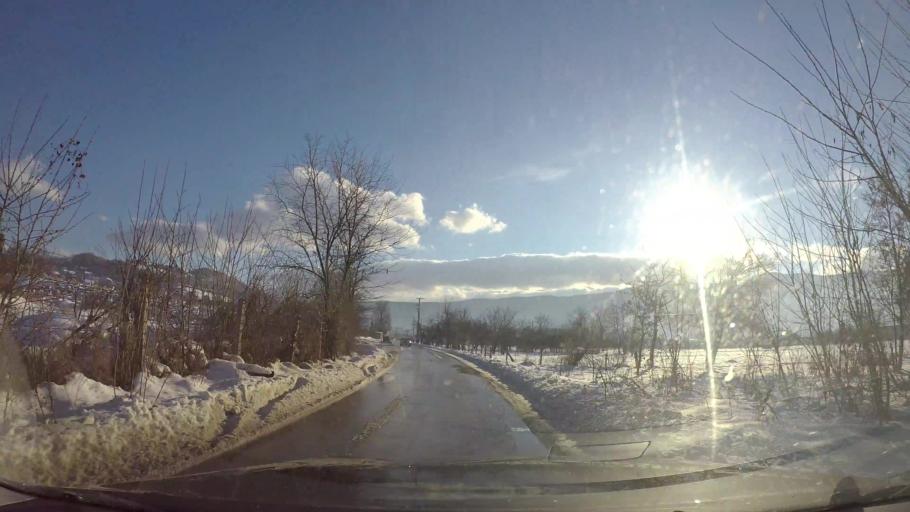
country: BA
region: Federation of Bosnia and Herzegovina
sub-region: Kanton Sarajevo
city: Sarajevo
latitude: 43.8133
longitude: 18.3462
